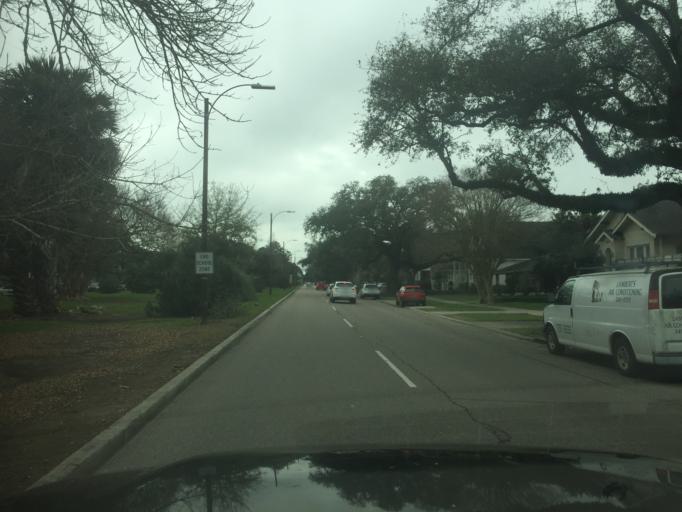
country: US
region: Louisiana
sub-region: Jefferson Parish
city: Metairie
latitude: 30.0066
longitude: -90.1080
